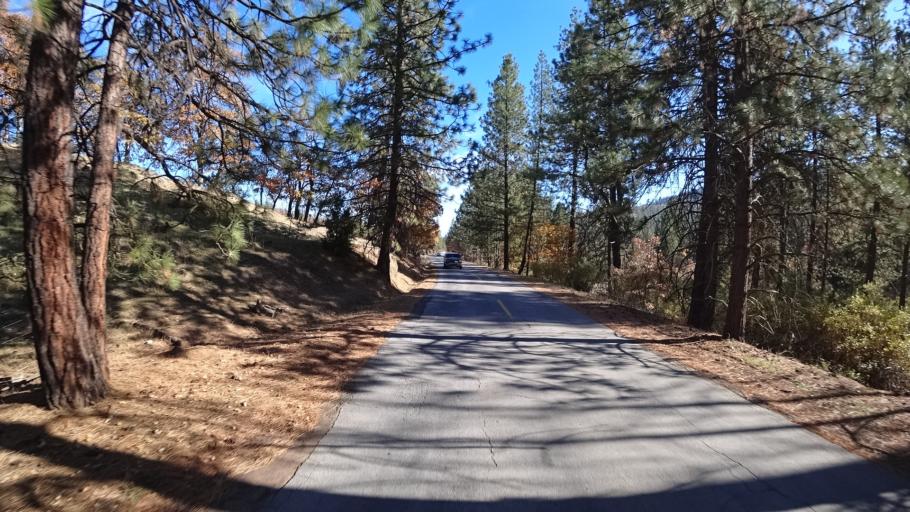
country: US
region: California
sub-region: Siskiyou County
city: Yreka
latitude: 41.7218
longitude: -122.6921
